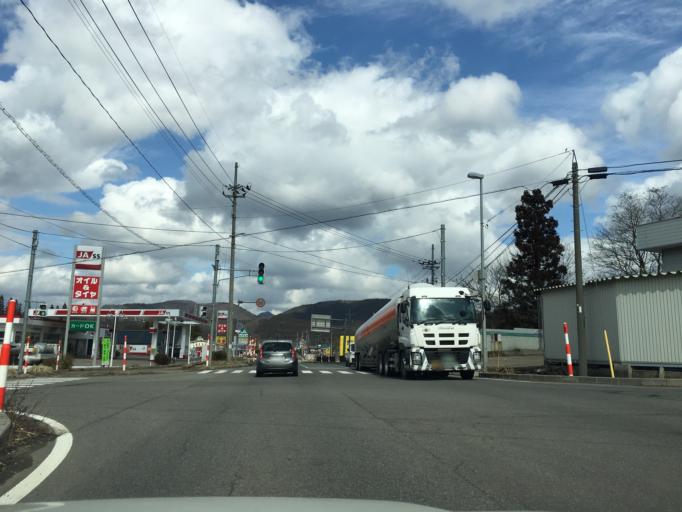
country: JP
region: Akita
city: Odate
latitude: 40.2166
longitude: 140.5842
